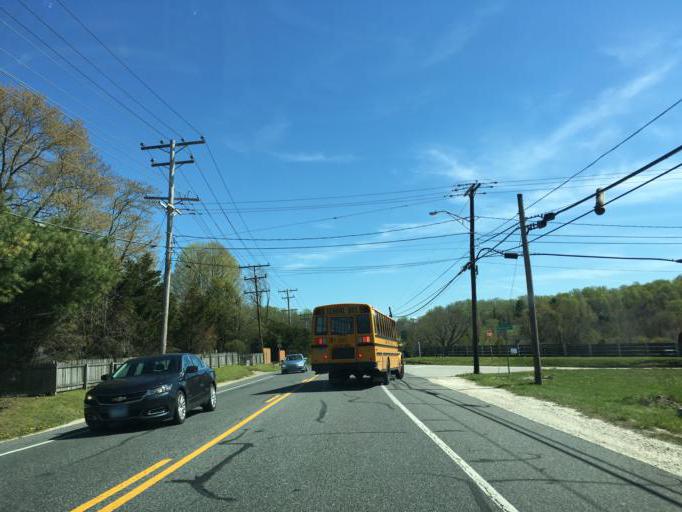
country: US
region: Maryland
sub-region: Baltimore County
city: Hunt Valley
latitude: 39.5425
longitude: -76.6498
